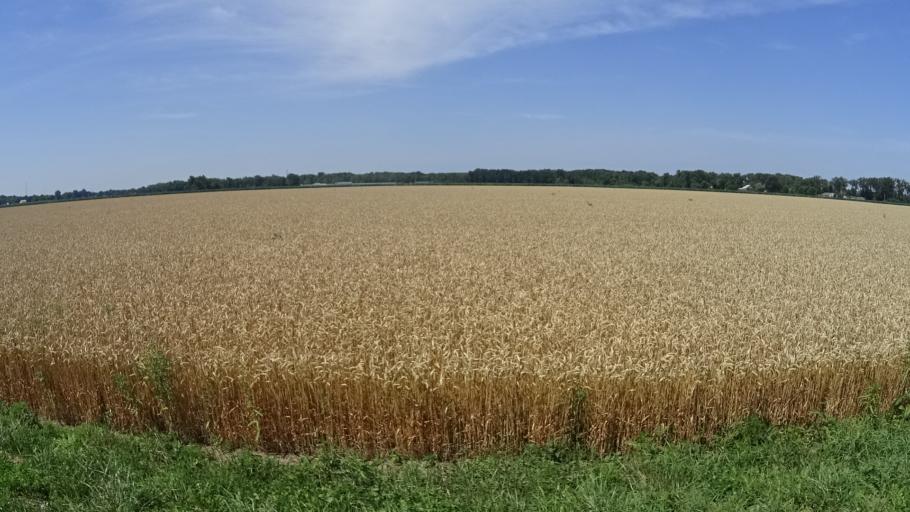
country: US
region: Ohio
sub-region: Erie County
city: Sandusky
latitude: 41.4193
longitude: -82.7902
